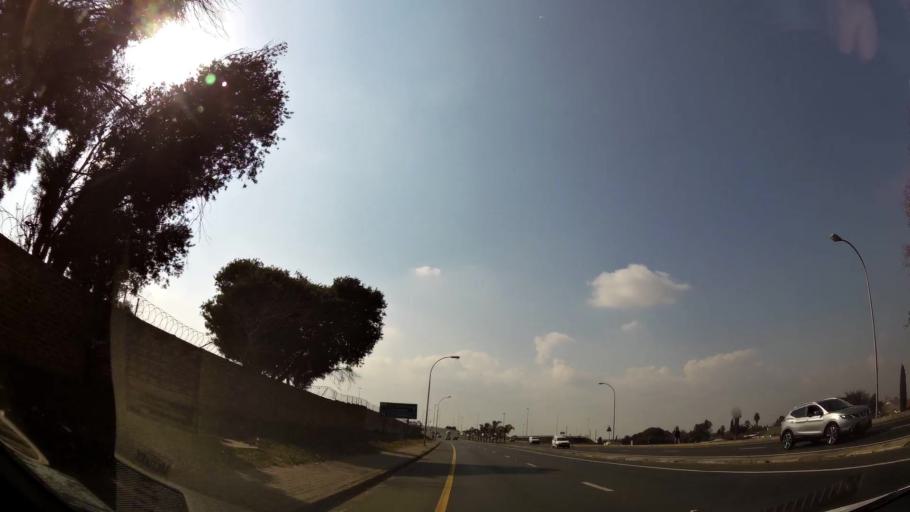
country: ZA
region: Gauteng
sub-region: Ekurhuleni Metropolitan Municipality
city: Germiston
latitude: -26.1773
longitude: 28.1947
